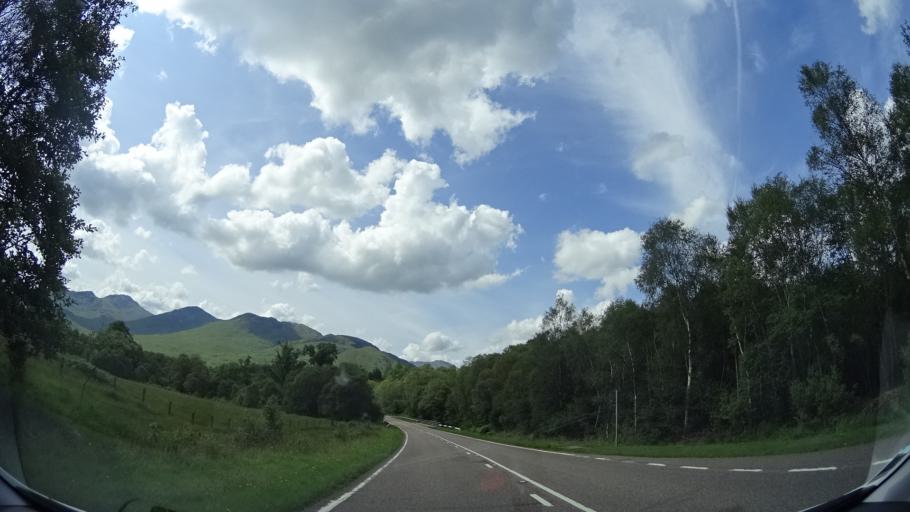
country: GB
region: Scotland
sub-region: Highland
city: Fort William
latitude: 56.8647
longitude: -5.3929
